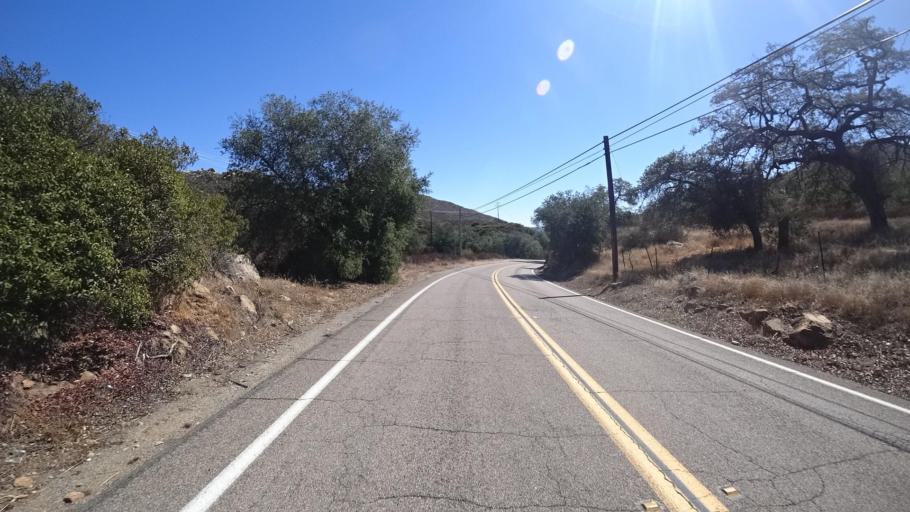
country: US
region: California
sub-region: San Diego County
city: Alpine
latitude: 32.7116
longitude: -116.7445
